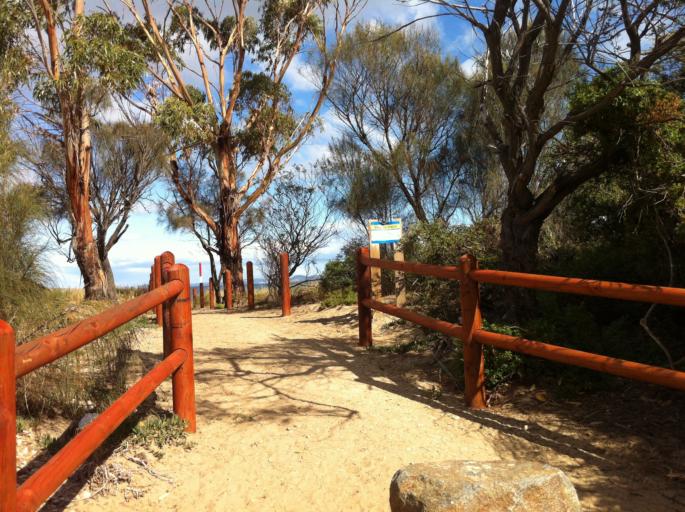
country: AU
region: Tasmania
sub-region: Clarence
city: Bellerive
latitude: -42.8788
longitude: 147.3822
